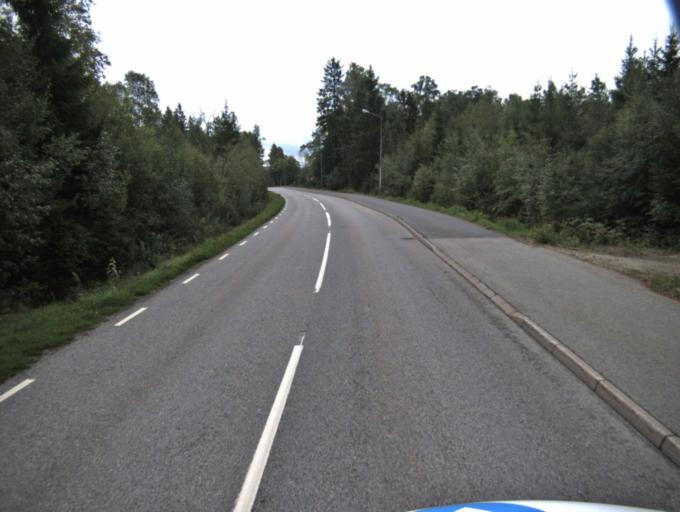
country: SE
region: Vaestra Goetaland
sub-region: Ulricehamns Kommun
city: Ulricehamn
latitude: 57.7730
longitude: 13.4363
